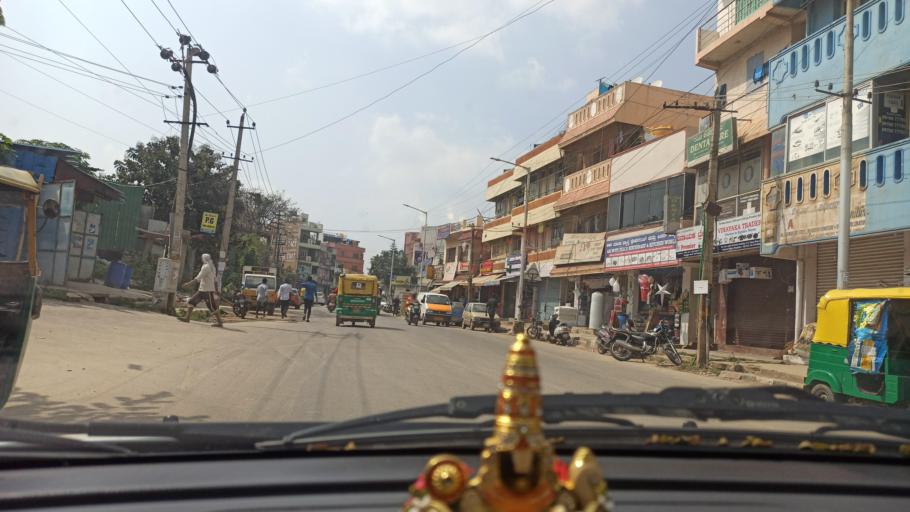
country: IN
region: Karnataka
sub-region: Bangalore Urban
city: Bangalore
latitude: 13.0146
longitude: 77.6655
